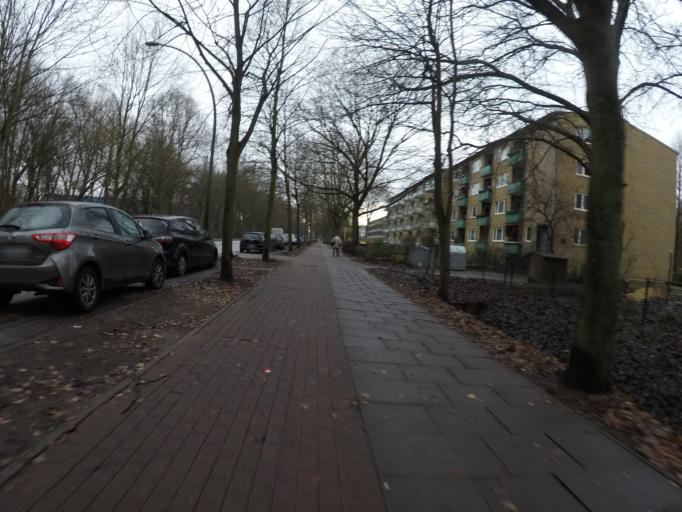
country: DE
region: Hamburg
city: Harburg
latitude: 53.4897
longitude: 9.9903
